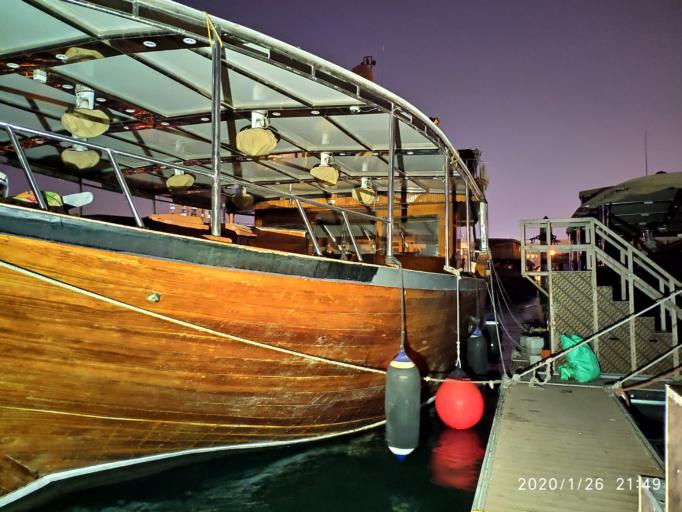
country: QA
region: Baladiyat ad Dawhah
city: Doha
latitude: 25.2934
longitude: 51.5373
